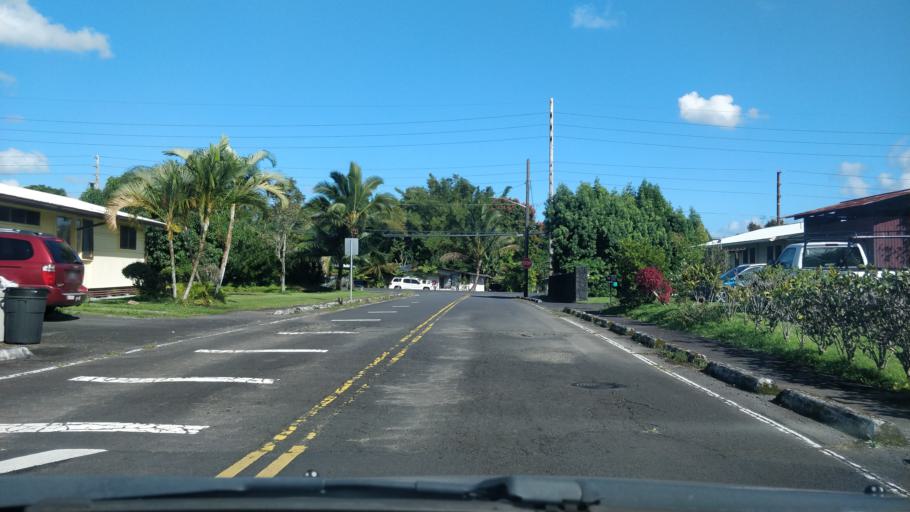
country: US
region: Hawaii
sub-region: Hawaii County
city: Hilo
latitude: 19.6827
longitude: -155.0868
